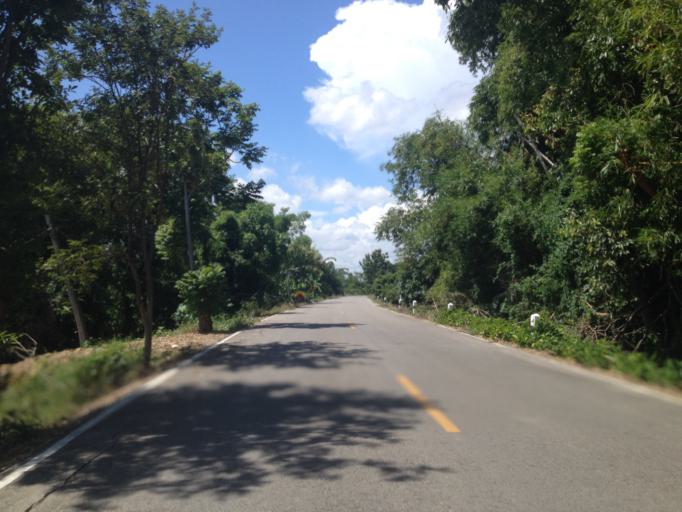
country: TH
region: Lamphun
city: Lamphun
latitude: 18.6055
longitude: 98.9676
